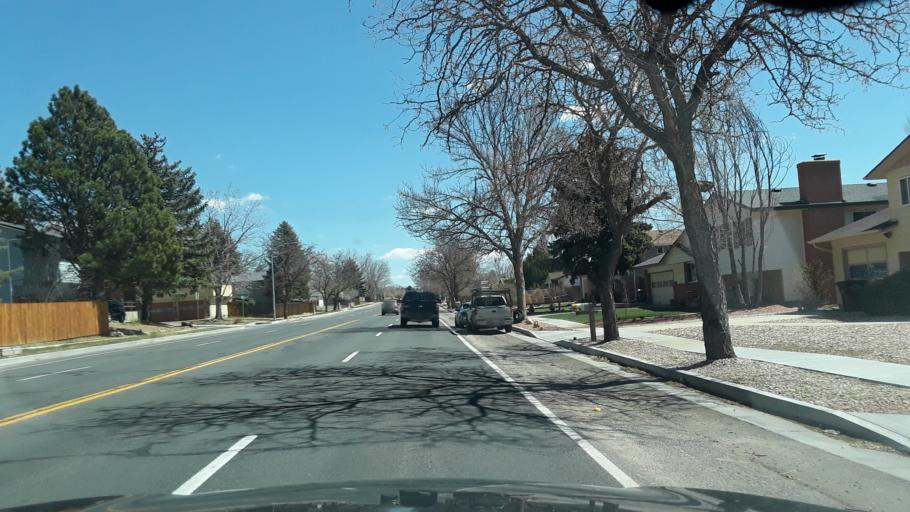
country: US
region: Colorado
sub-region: El Paso County
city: Cimarron Hills
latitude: 38.8543
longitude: -104.7430
